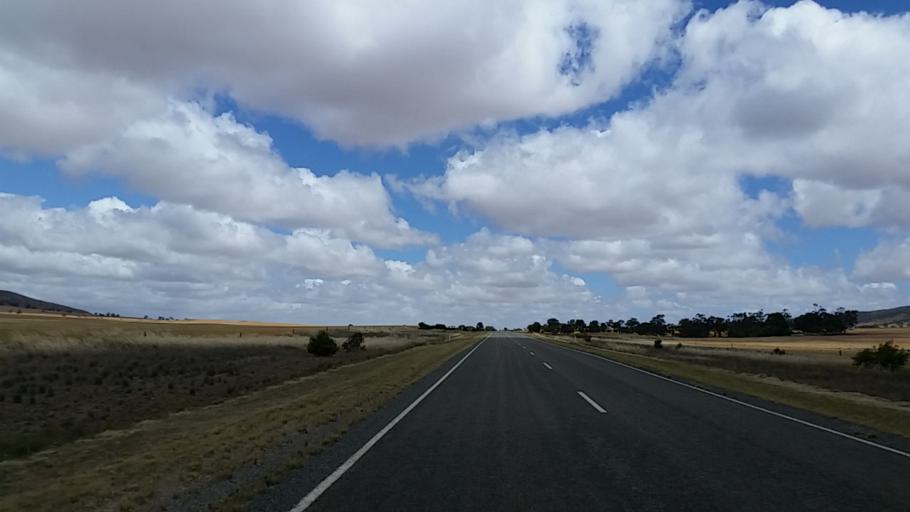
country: AU
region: South Australia
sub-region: Peterborough
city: Peterborough
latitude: -32.8571
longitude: 138.5440
